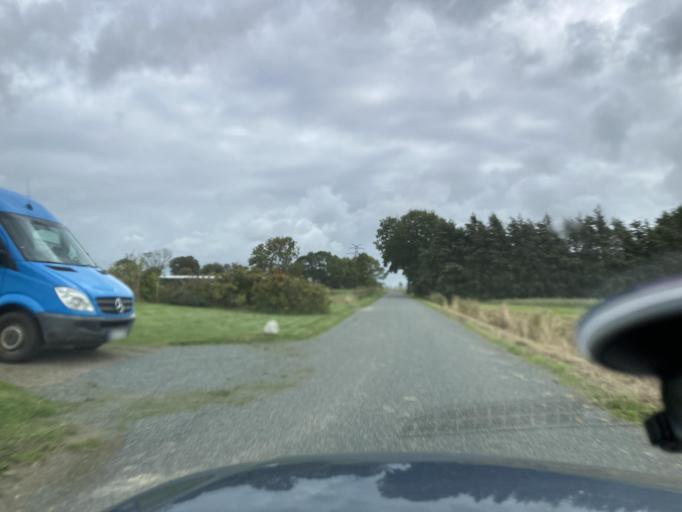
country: DE
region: Schleswig-Holstein
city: Oesterwurth
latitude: 54.1944
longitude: 8.9773
